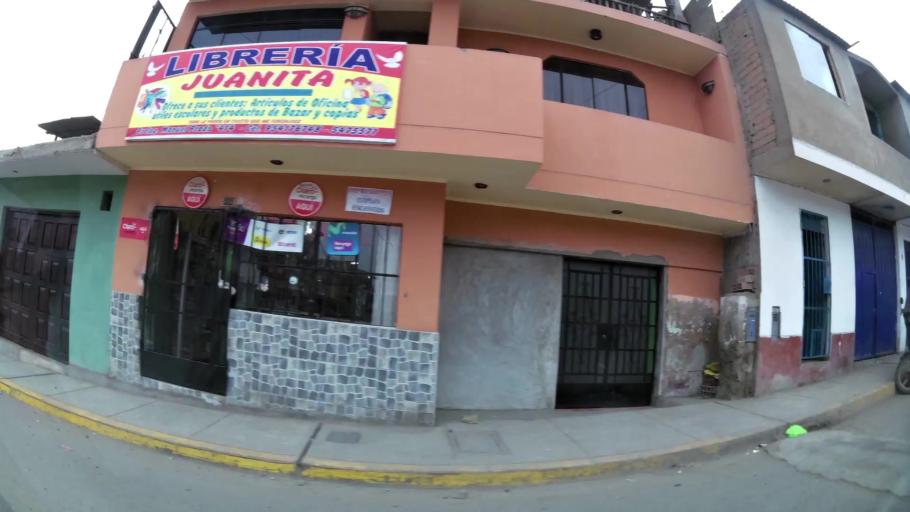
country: PE
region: Lima
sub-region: Lima
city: Urb. Santo Domingo
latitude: -11.8716
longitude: -77.0188
